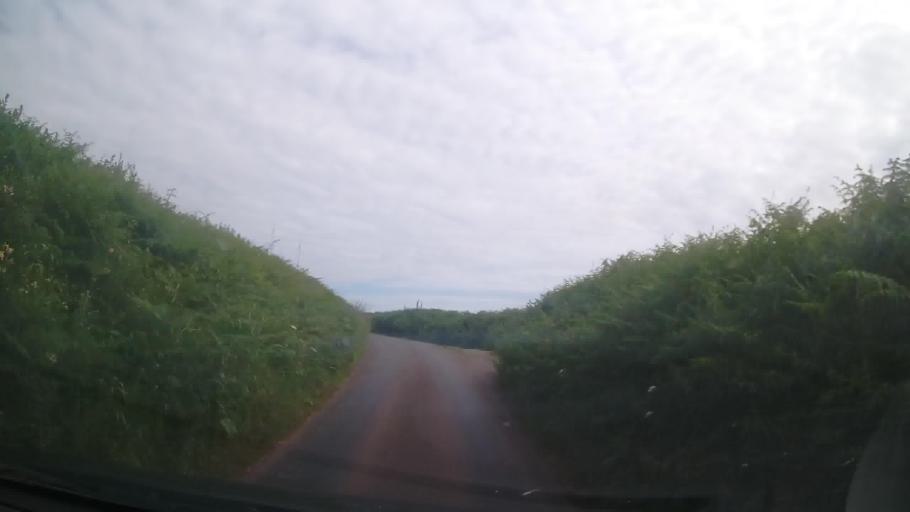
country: GB
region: England
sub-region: Devon
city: Salcombe
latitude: 50.2334
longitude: -3.6711
